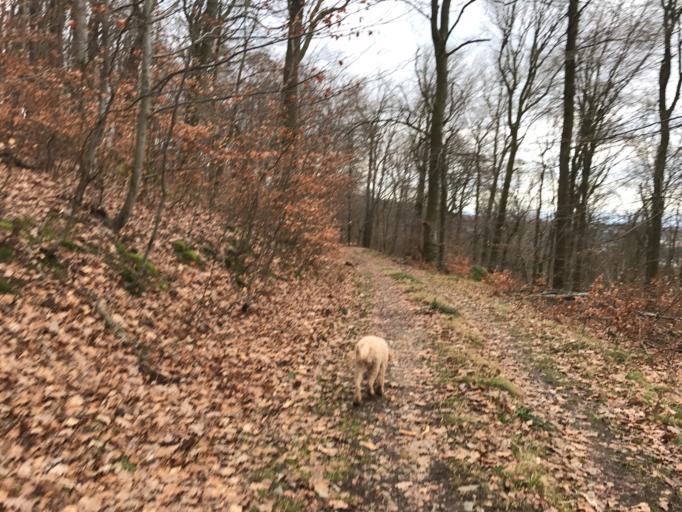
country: DE
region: Hesse
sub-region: Regierungsbezirk Darmstadt
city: Konigstein im Taunus
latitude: 50.1975
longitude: 8.4608
